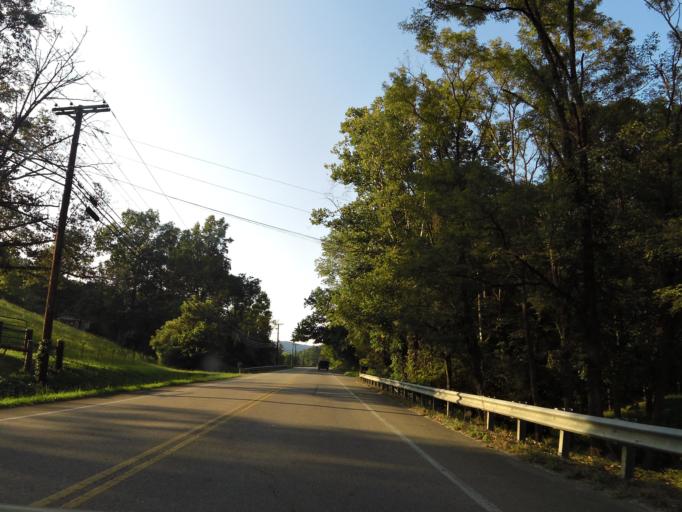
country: US
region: Tennessee
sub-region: Knox County
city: Mascot
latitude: 36.0796
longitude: -83.7432
